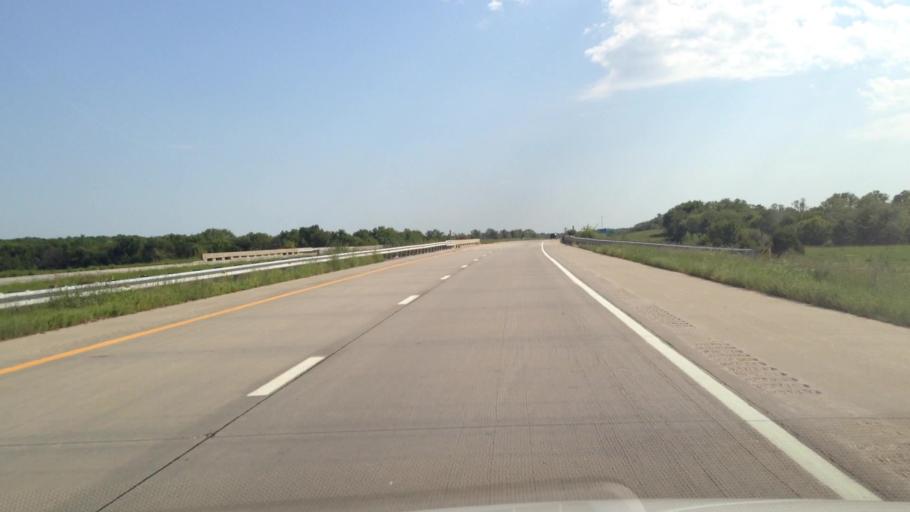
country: US
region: Kansas
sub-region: Miami County
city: Louisburg
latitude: 38.5353
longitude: -94.6846
